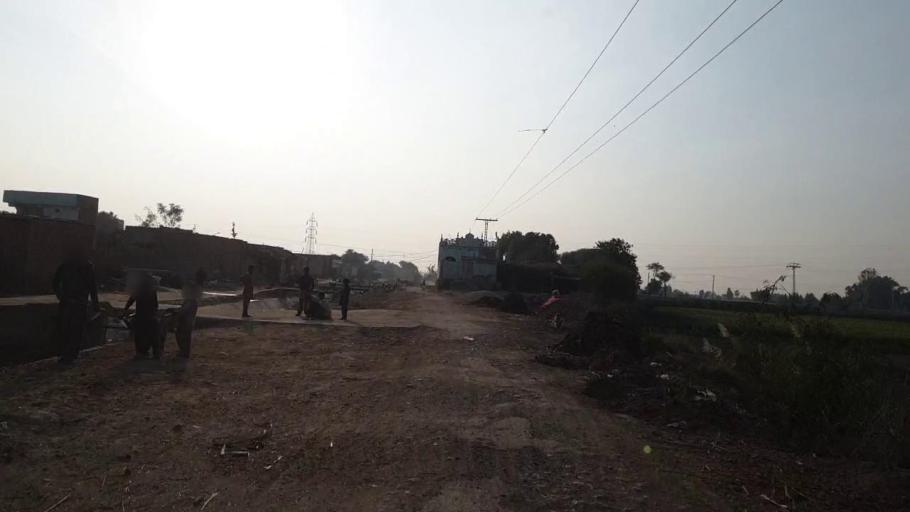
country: PK
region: Sindh
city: Matiari
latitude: 25.5870
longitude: 68.4531
